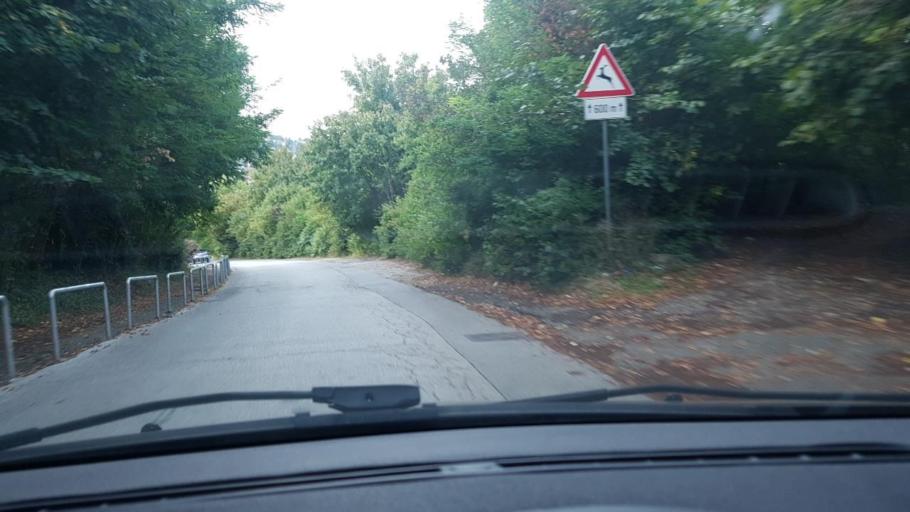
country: HR
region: Grad Zagreb
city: Zagreb
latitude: 45.8576
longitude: 15.9488
